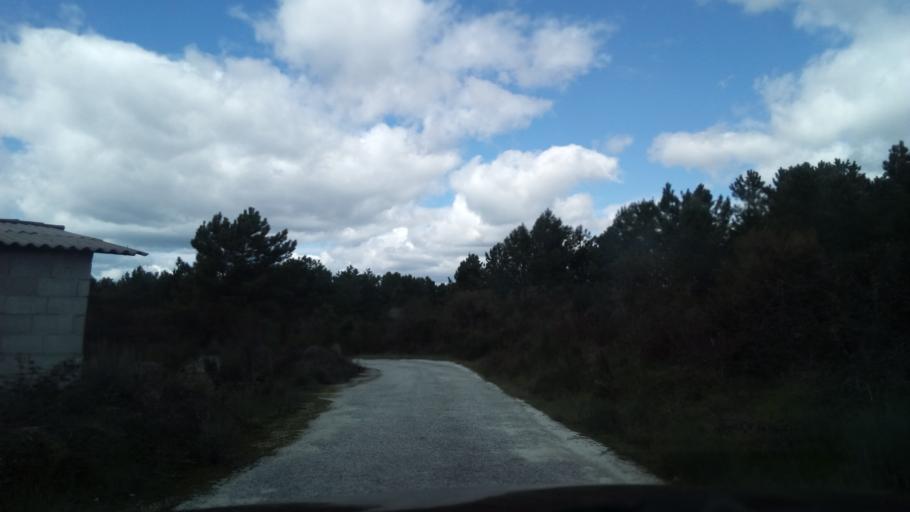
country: PT
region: Guarda
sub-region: Fornos de Algodres
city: Fornos de Algodres
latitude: 40.6684
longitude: -7.5033
